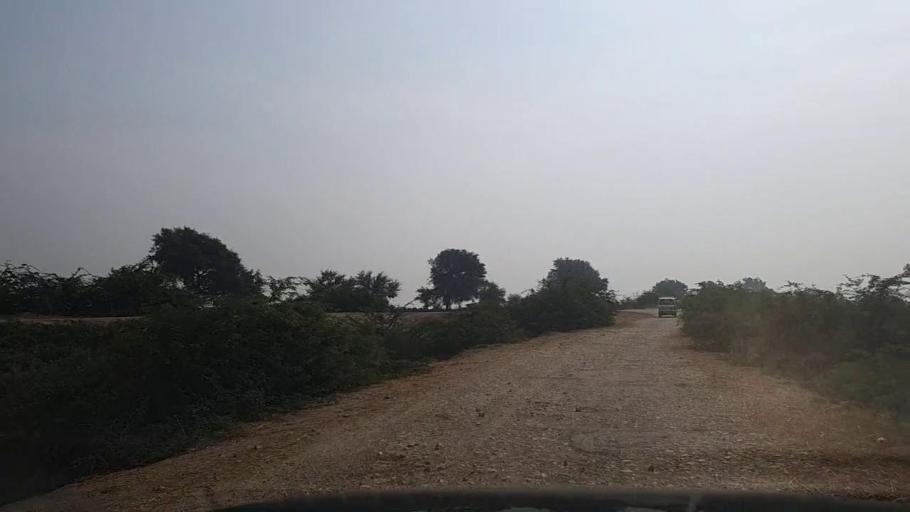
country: PK
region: Sindh
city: Mirpur Sakro
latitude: 24.3758
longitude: 67.7560
